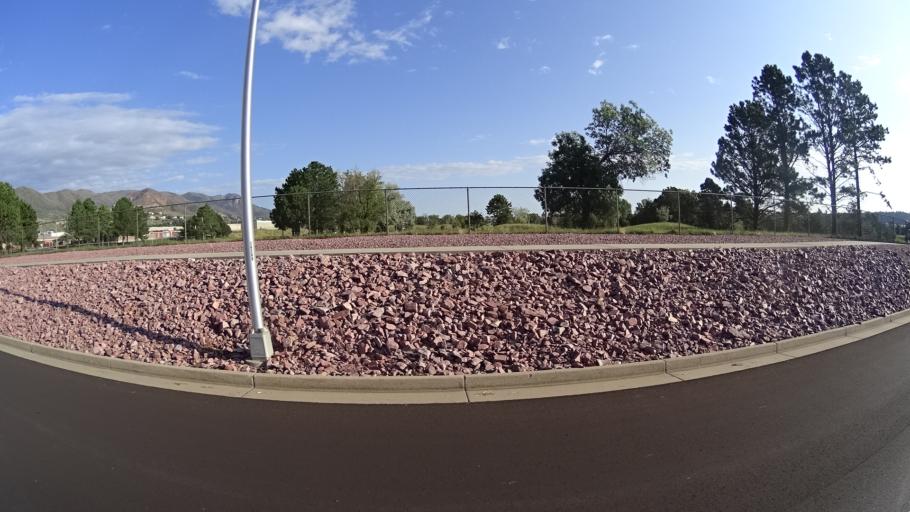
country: US
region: Colorado
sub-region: El Paso County
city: Manitou Springs
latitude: 38.8967
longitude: -104.8650
